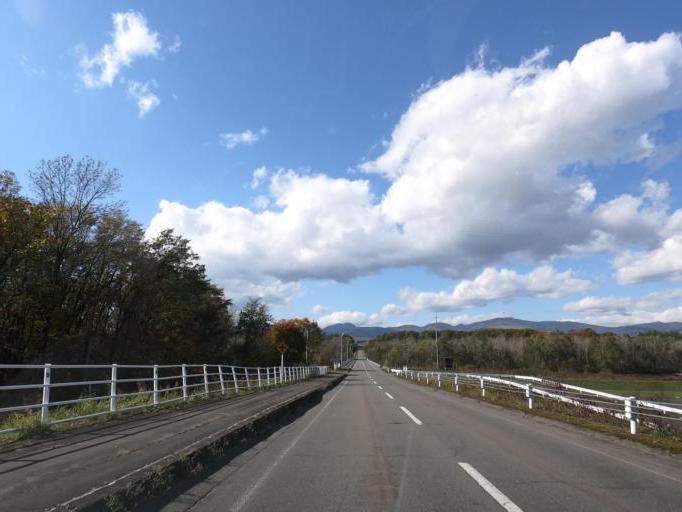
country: JP
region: Hokkaido
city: Otofuke
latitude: 43.2376
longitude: 143.2747
